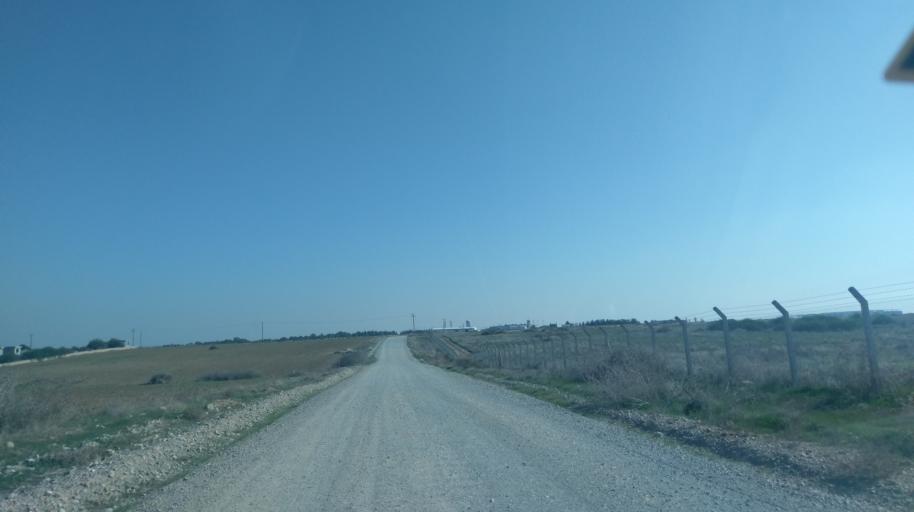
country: CY
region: Lefkosia
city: Geri
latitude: 35.1637
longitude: 33.4894
